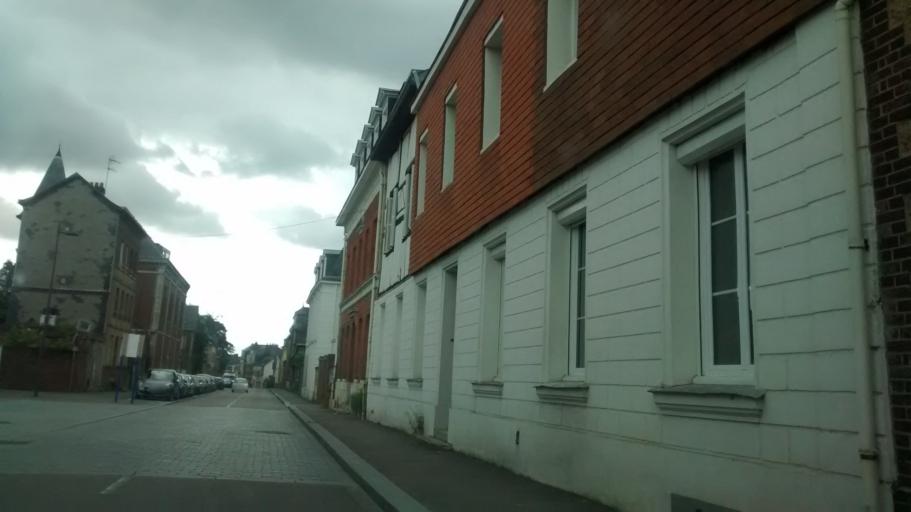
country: FR
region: Haute-Normandie
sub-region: Departement de la Seine-Maritime
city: Mont-Saint-Aignan
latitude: 49.4592
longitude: 1.0804
